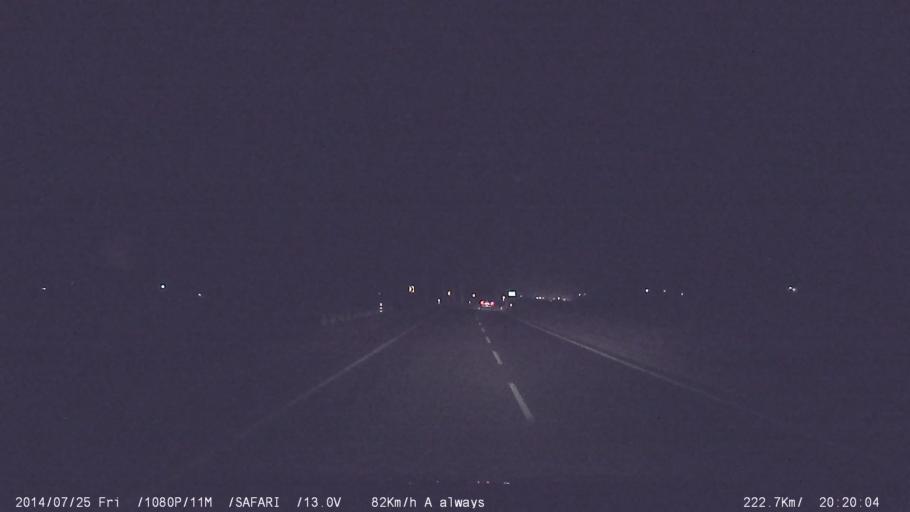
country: IN
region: Tamil Nadu
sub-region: Salem
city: Konganapuram
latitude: 11.5227
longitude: 77.9420
